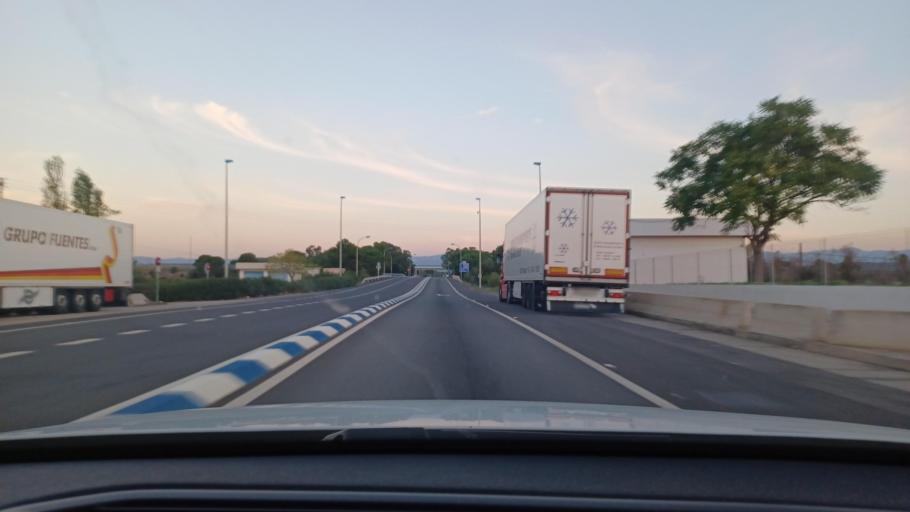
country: ES
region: Catalonia
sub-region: Provincia de Tarragona
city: Ulldecona
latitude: 40.5546
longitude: 0.4301
